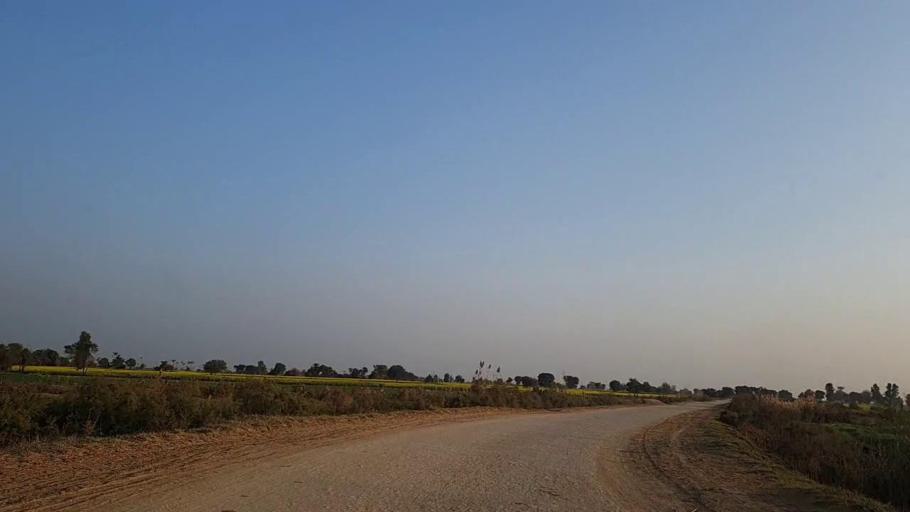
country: PK
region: Sindh
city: Shahdadpur
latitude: 26.0212
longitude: 68.4886
